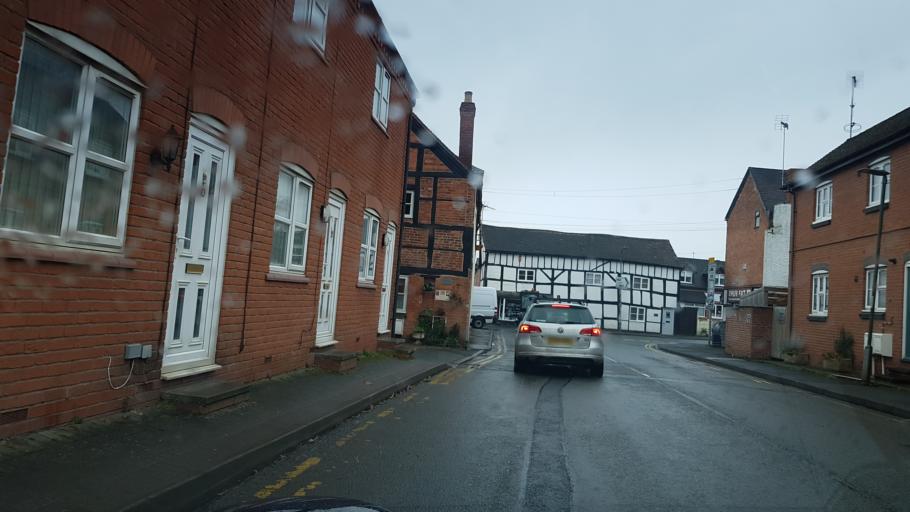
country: GB
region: England
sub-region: Herefordshire
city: Bromyard
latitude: 52.1901
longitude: -2.5090
